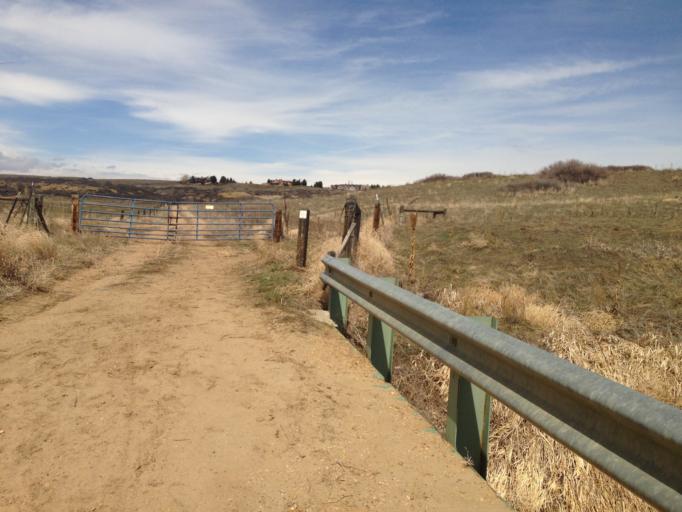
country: US
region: Colorado
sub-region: Boulder County
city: Gunbarrel
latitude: 40.0524
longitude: -105.1444
